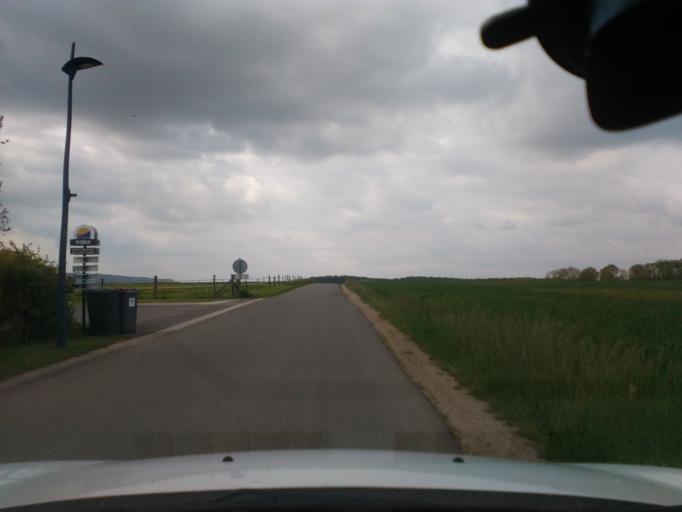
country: FR
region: Lorraine
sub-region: Departement des Vosges
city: Mirecourt
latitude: 48.3384
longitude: 6.1003
